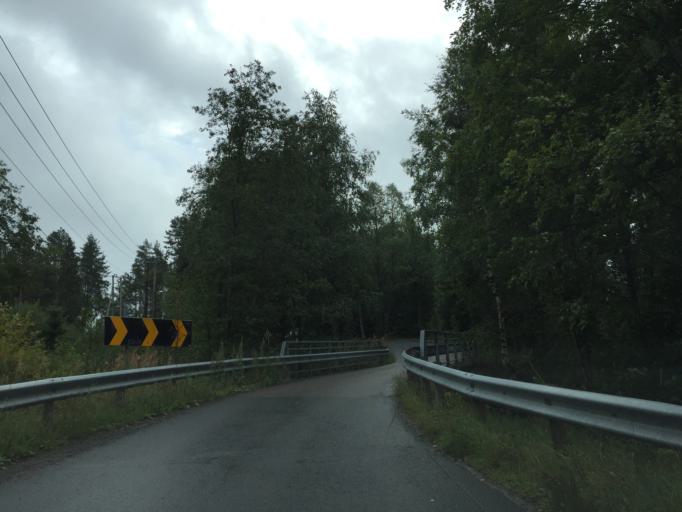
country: NO
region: Akershus
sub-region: Baerum
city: Lysaker
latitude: 60.0182
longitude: 10.6187
